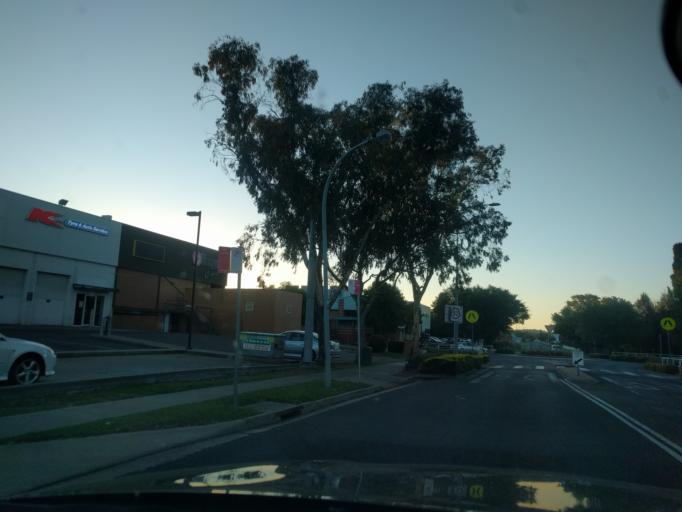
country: AU
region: New South Wales
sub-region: Armidale Dumaresq
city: Armidale
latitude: -30.5112
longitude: 151.6648
